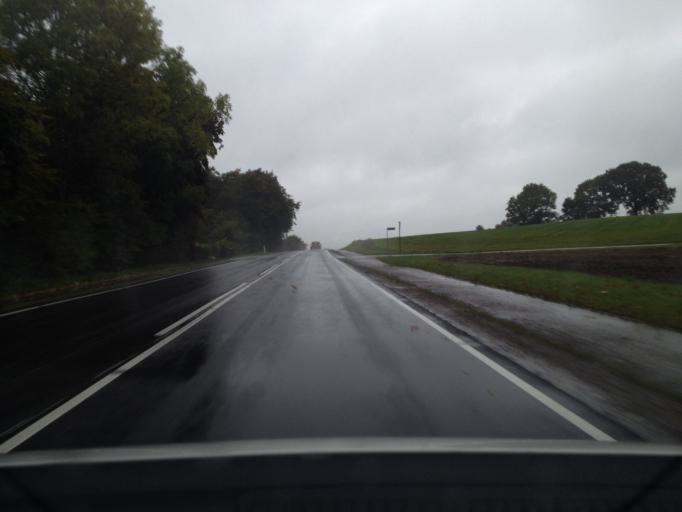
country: DK
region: Zealand
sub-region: Holbaek Kommune
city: Tollose
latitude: 55.5325
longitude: 11.7168
